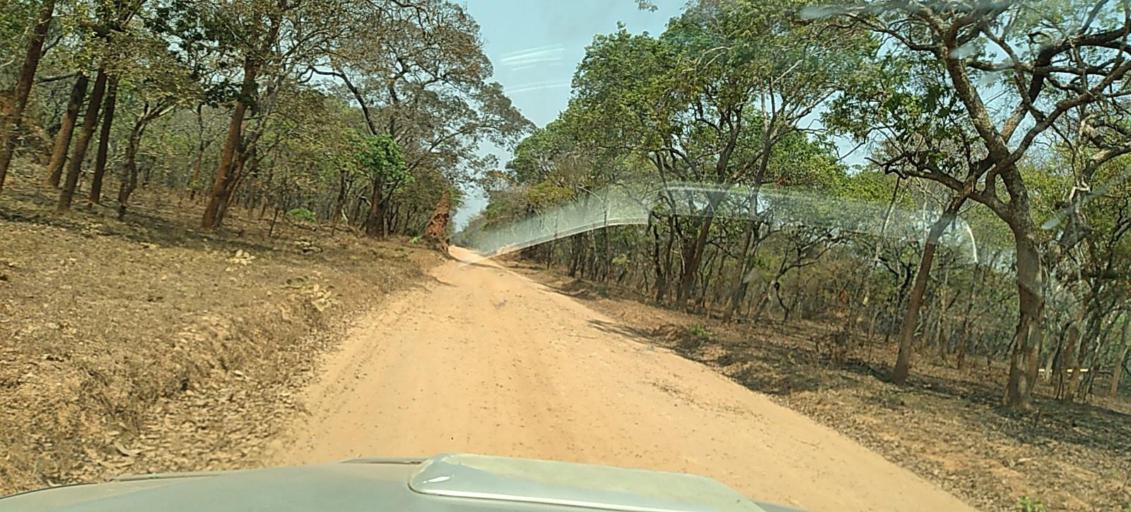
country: ZM
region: North-Western
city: Kasempa
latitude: -13.6607
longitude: 26.2701
